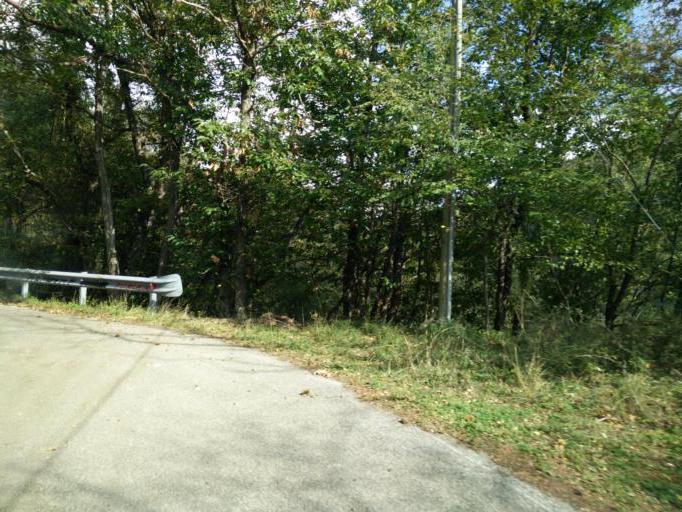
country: IT
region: Liguria
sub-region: Provincia di La Spezia
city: Sesta Godano
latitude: 44.3439
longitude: 9.7041
